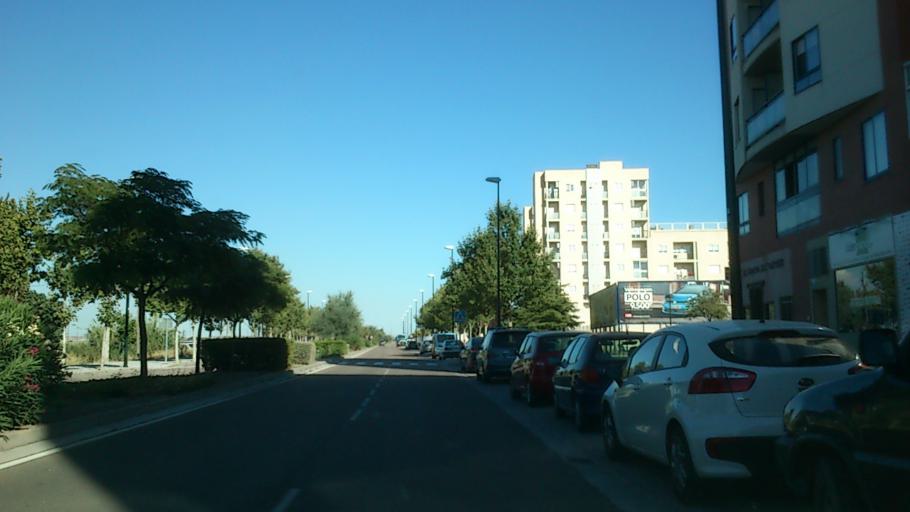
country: ES
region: Aragon
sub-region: Provincia de Zaragoza
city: Zaragoza
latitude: 41.6705
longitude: -0.8253
